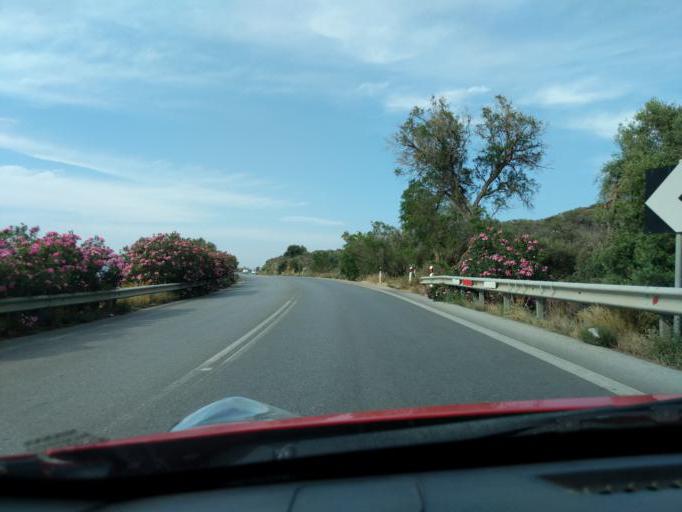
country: GR
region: Crete
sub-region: Nomos Rethymnis
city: Atsipopoulon
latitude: 35.3577
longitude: 24.3717
